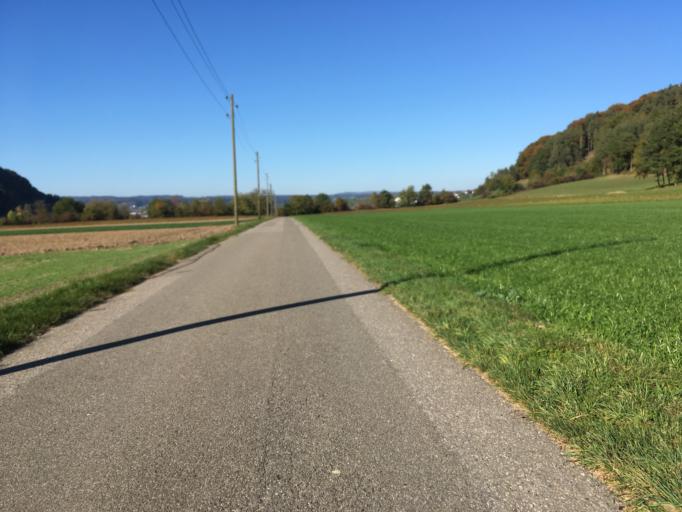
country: CH
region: Zurich
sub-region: Bezirk Buelach
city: Seglingen
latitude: 47.5581
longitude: 8.5281
